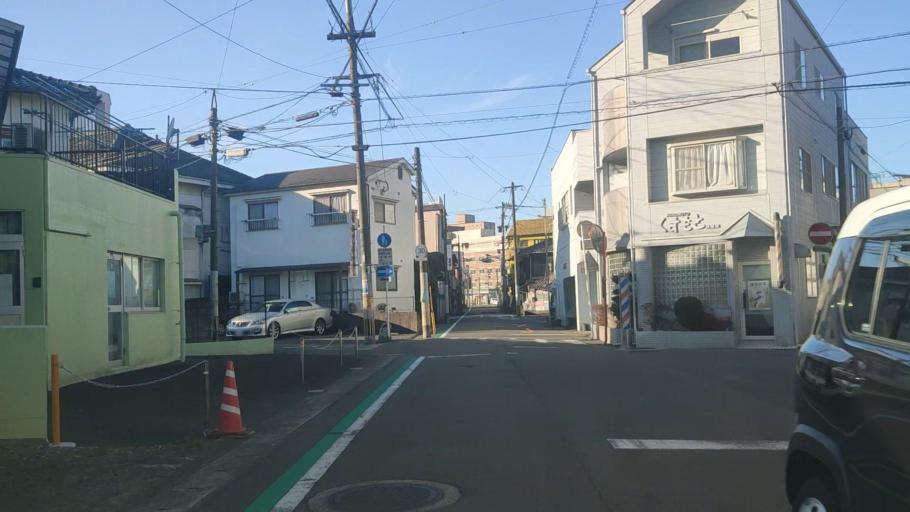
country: JP
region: Oita
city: Beppu
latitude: 33.2718
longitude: 131.5047
